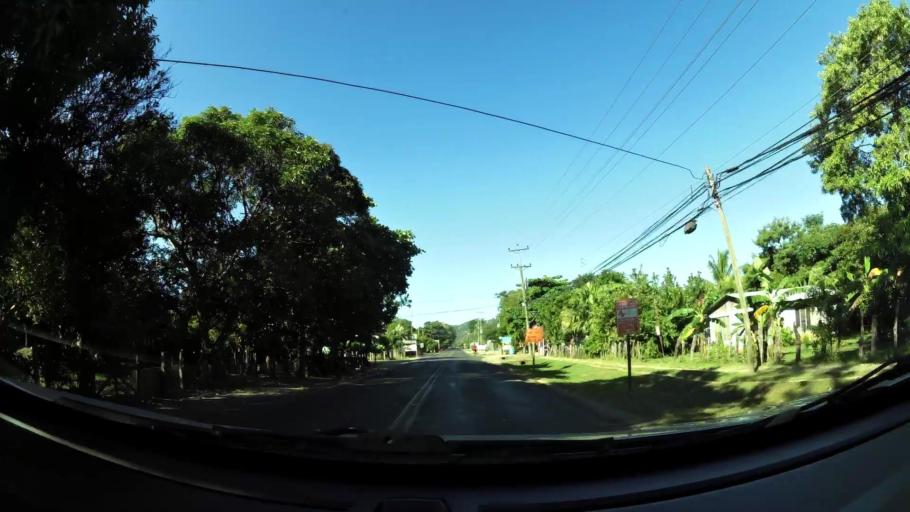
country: CR
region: Guanacaste
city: Belen
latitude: 10.4039
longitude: -85.5882
